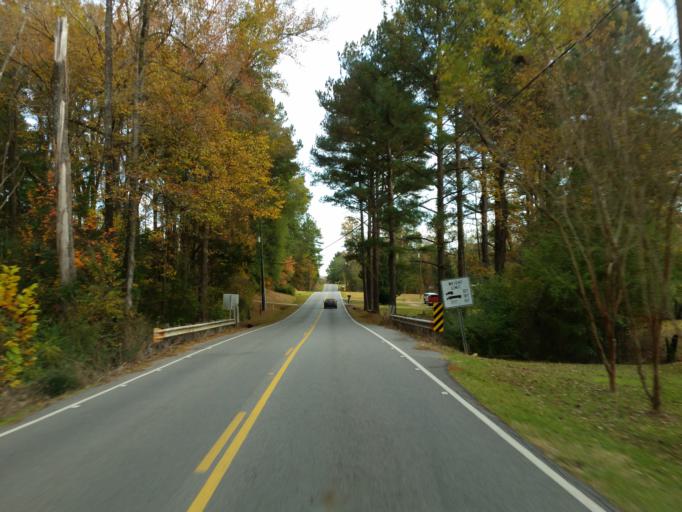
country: US
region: Mississippi
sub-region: Lauderdale County
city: Marion
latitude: 32.4077
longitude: -88.6054
